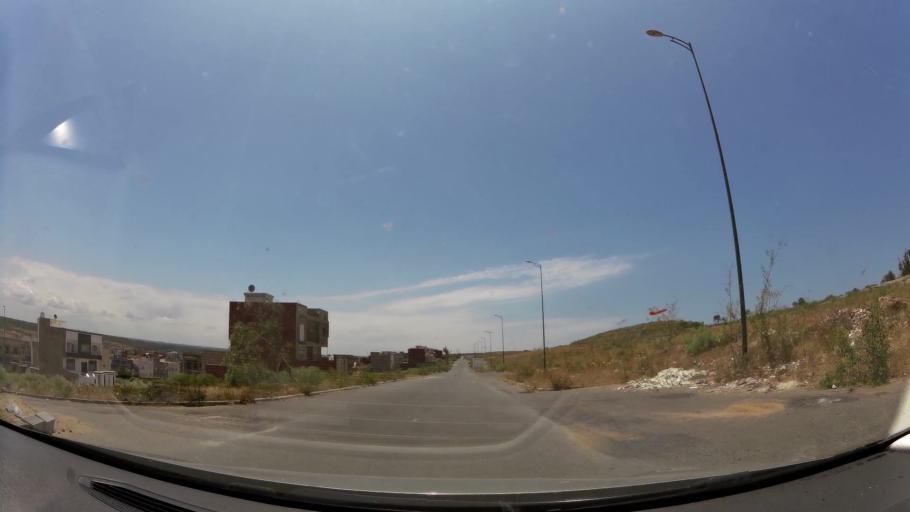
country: MA
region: Gharb-Chrarda-Beni Hssen
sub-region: Kenitra Province
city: Kenitra
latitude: 34.2522
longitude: -6.6588
